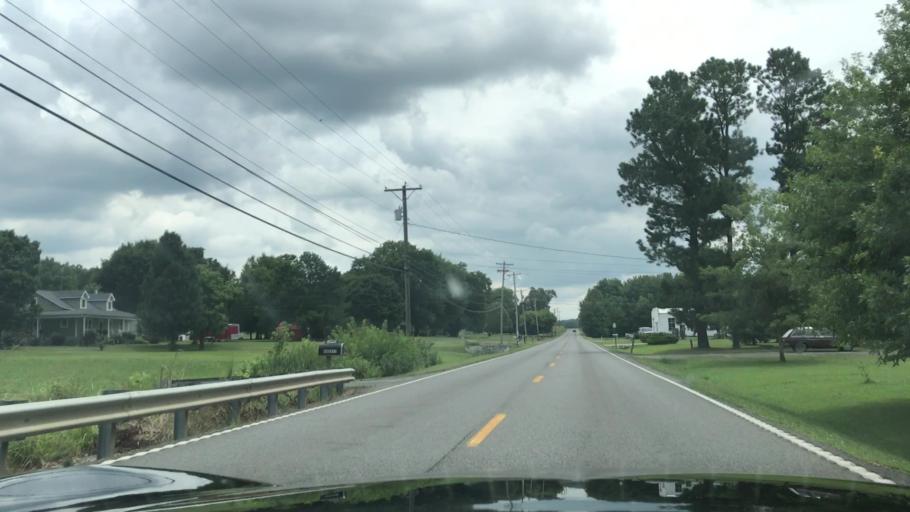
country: US
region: Kentucky
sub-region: Muhlenberg County
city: Greenville
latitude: 37.2014
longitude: -87.1380
